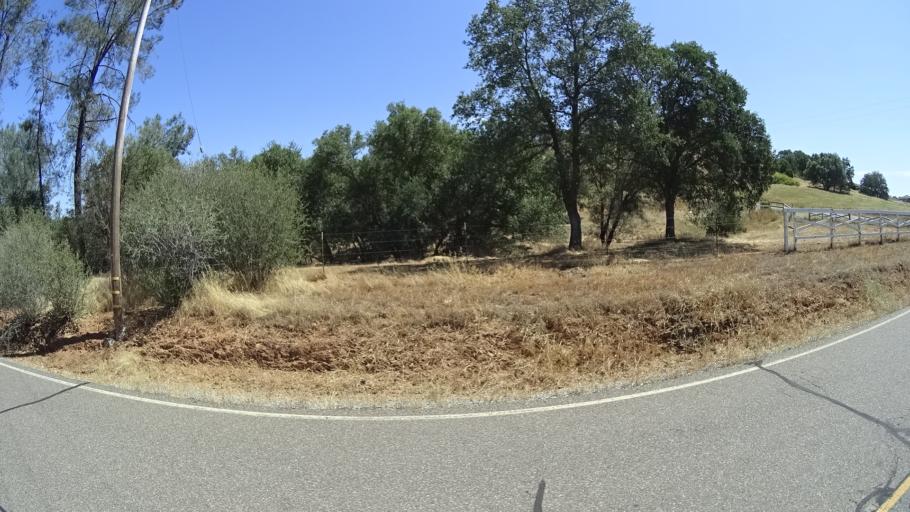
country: US
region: California
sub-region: Calaveras County
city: Copperopolis
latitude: 37.9459
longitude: -120.6152
